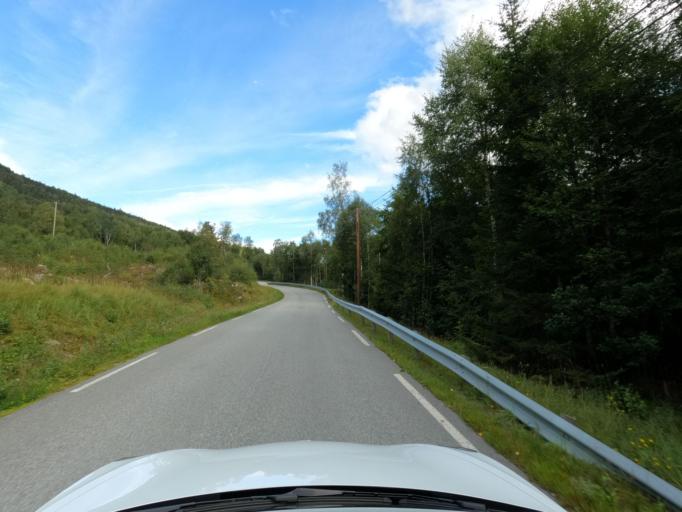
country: NO
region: Telemark
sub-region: Tinn
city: Rjukan
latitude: 60.0084
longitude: 8.7443
